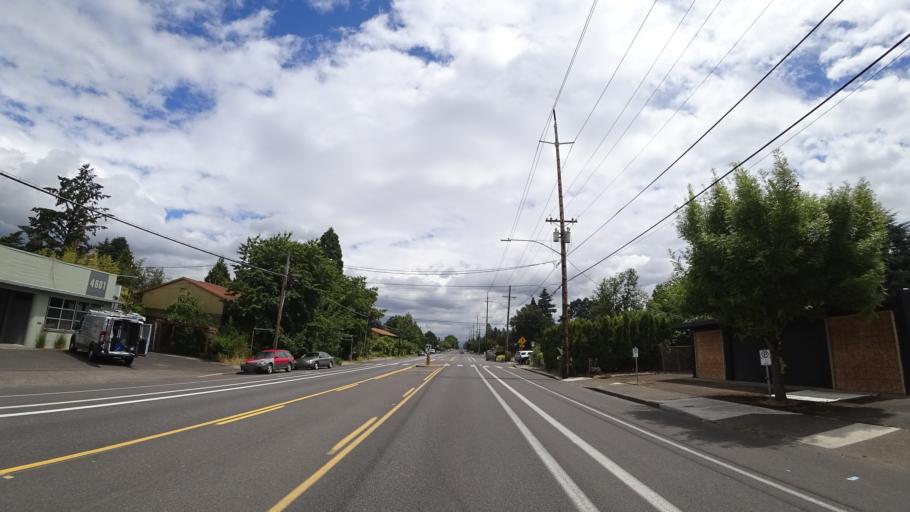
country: US
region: Oregon
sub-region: Multnomah County
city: Portland
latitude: 45.5627
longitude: -122.6157
